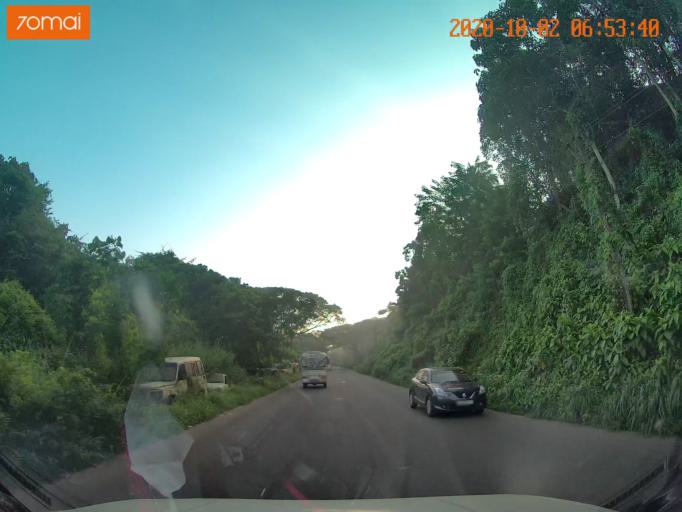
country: IN
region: Kerala
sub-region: Malappuram
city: Tirur
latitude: 10.8506
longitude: 76.0341
